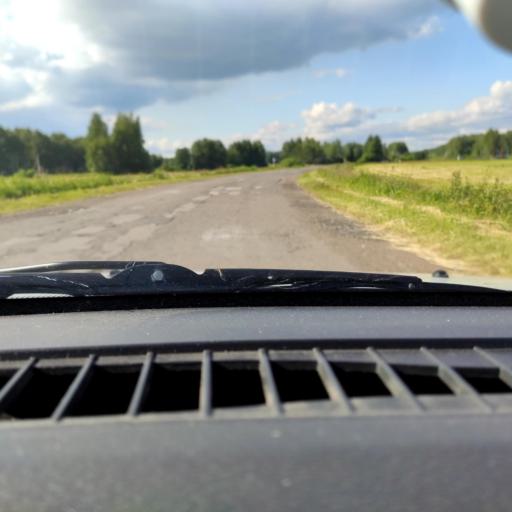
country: RU
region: Perm
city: Uinskoye
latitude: 57.2373
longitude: 56.5317
